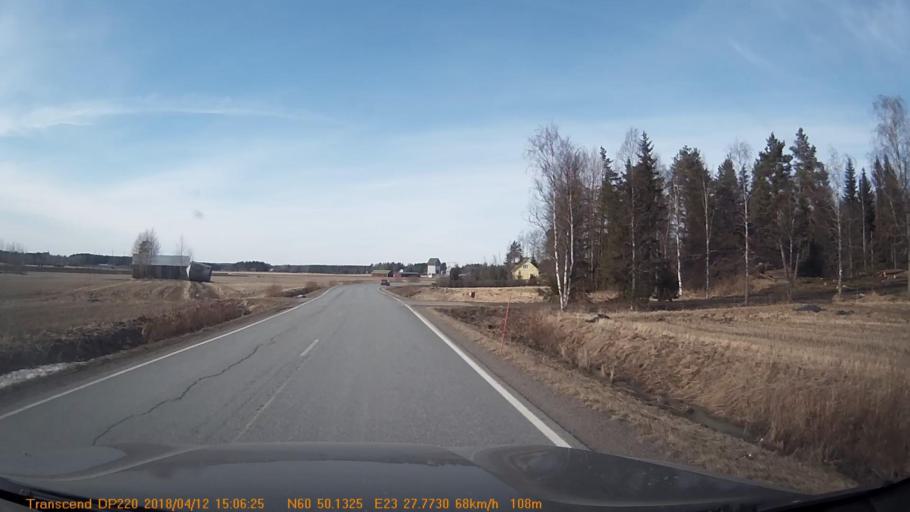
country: FI
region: Haeme
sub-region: Forssa
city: Jokioinen
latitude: 60.8360
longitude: 23.4623
